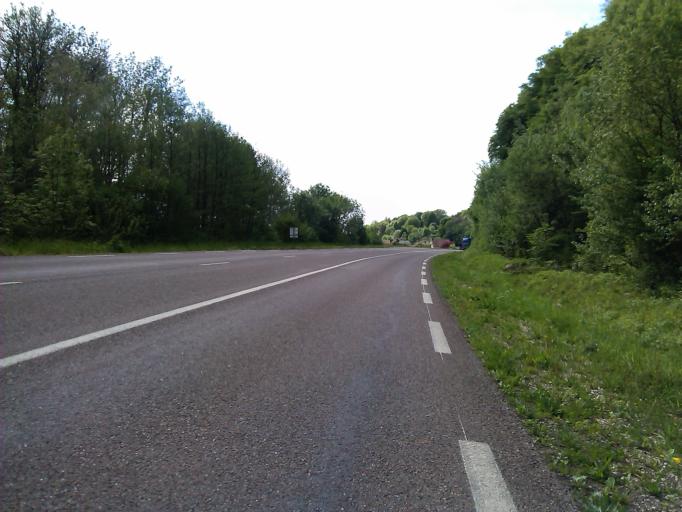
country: FR
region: Franche-Comte
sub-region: Departement du Doubs
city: Colombier-Fontaine
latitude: 47.4536
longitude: 6.6650
